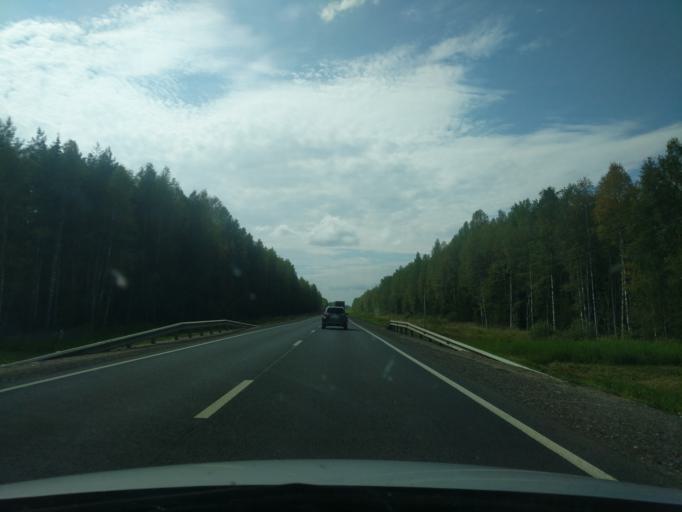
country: RU
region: Kostroma
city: Kadyy
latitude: 57.8069
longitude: 43.2177
